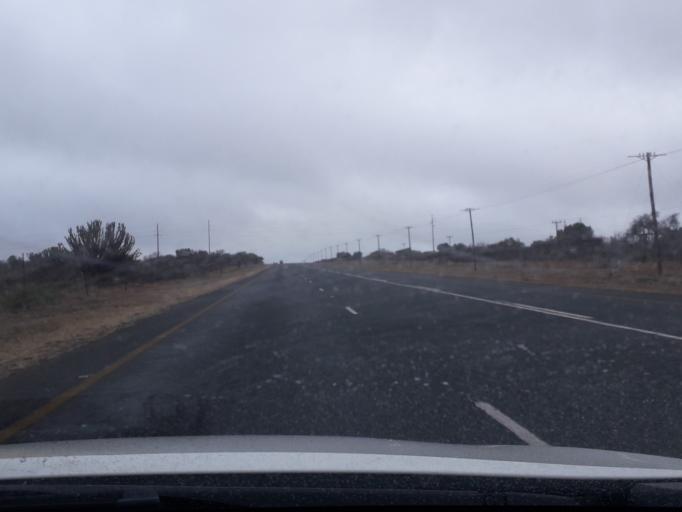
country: ZA
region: Limpopo
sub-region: Vhembe District Municipality
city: Louis Trichardt
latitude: -23.3809
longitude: 29.7668
